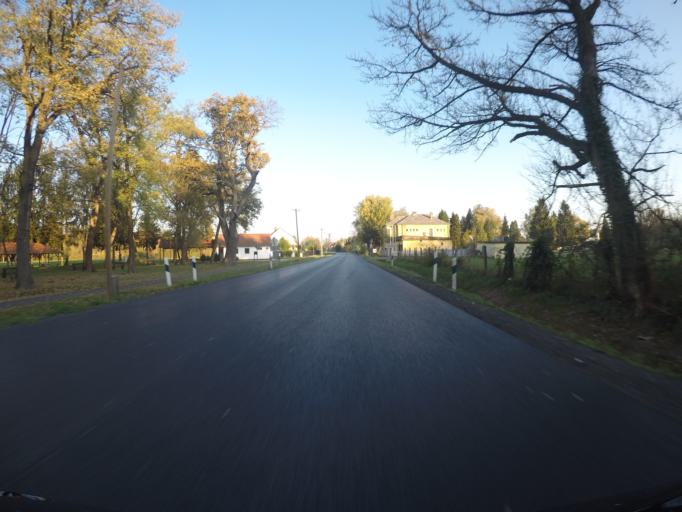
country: HU
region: Somogy
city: Barcs
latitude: 45.9795
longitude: 17.5830
